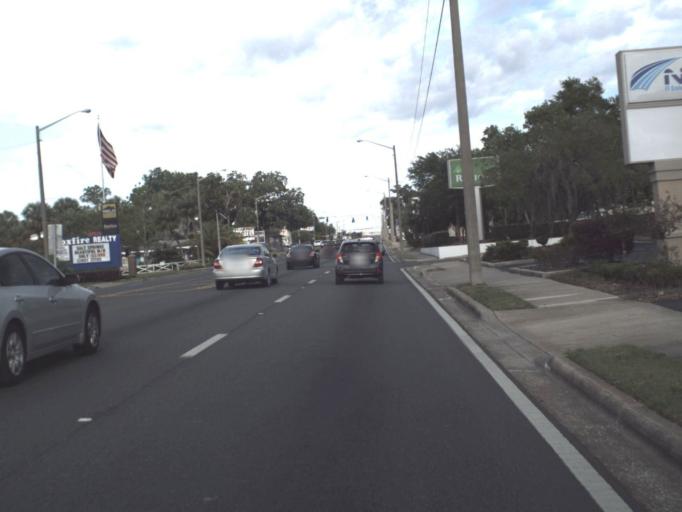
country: US
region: Florida
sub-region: Marion County
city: Ocala
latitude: 29.1870
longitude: -82.1326
